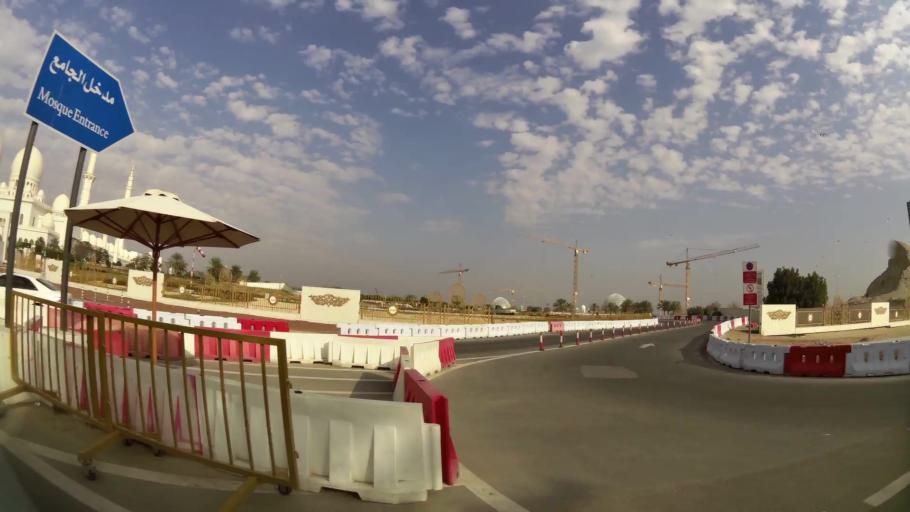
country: AE
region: Abu Dhabi
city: Abu Dhabi
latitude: 24.4096
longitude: 54.4718
